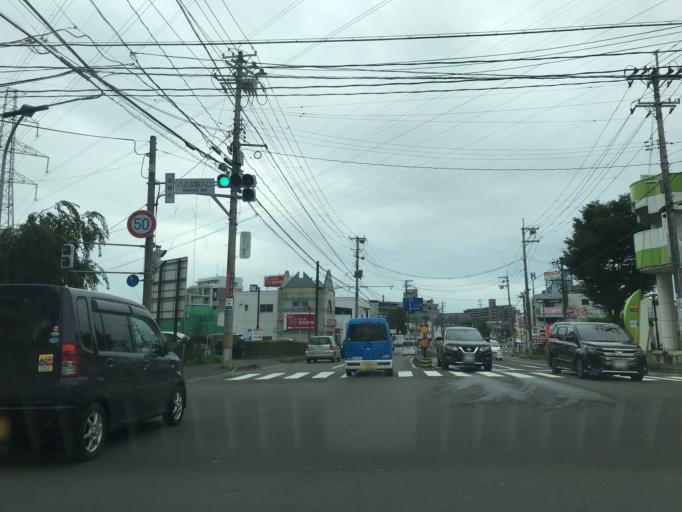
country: JP
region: Miyagi
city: Sendai-shi
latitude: 38.3141
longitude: 140.8845
